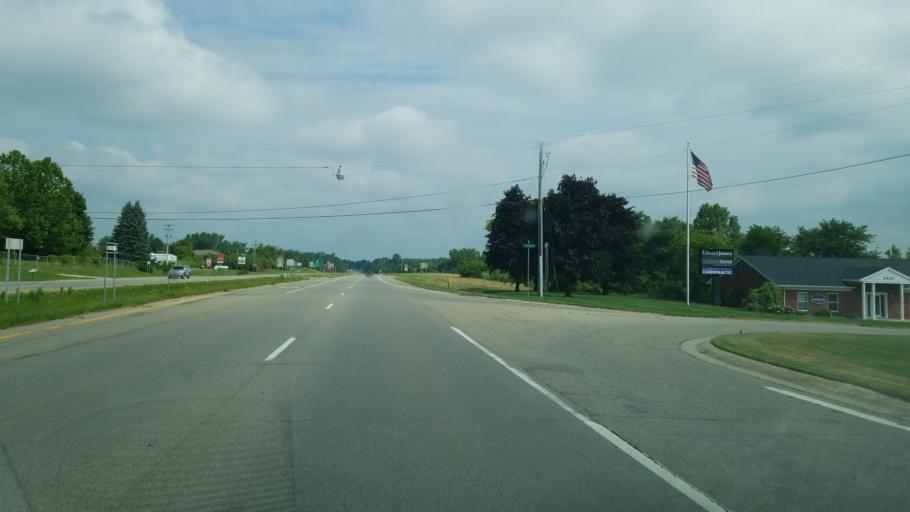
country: US
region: Michigan
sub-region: Kent County
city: Comstock Park
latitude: 43.0801
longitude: -85.6900
